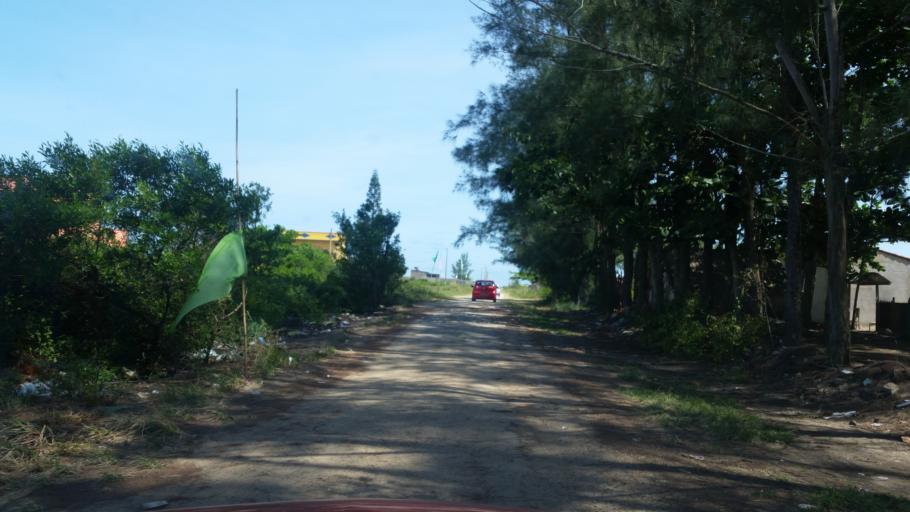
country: BR
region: Sao Paulo
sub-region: Iguape
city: Iguape
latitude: -24.6998
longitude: -47.4636
